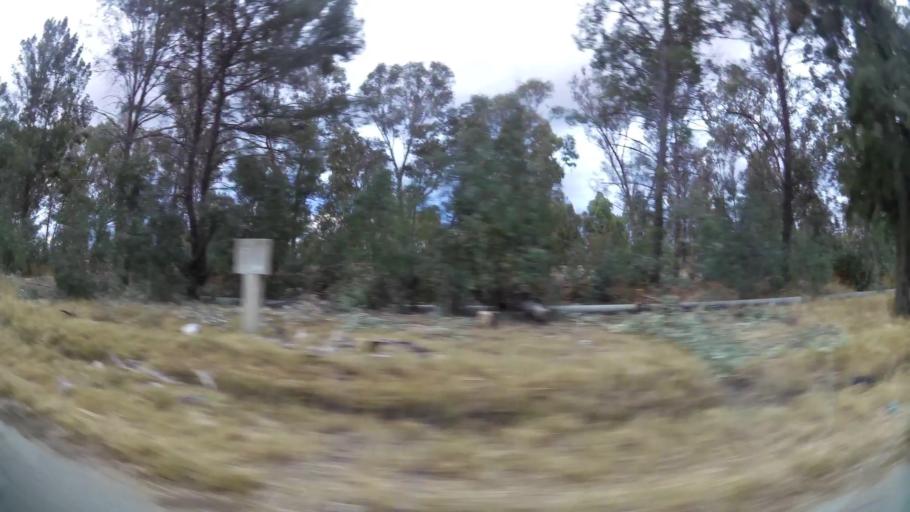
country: ZA
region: Orange Free State
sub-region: Lejweleputswa District Municipality
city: Welkom
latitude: -27.9629
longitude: 26.7098
